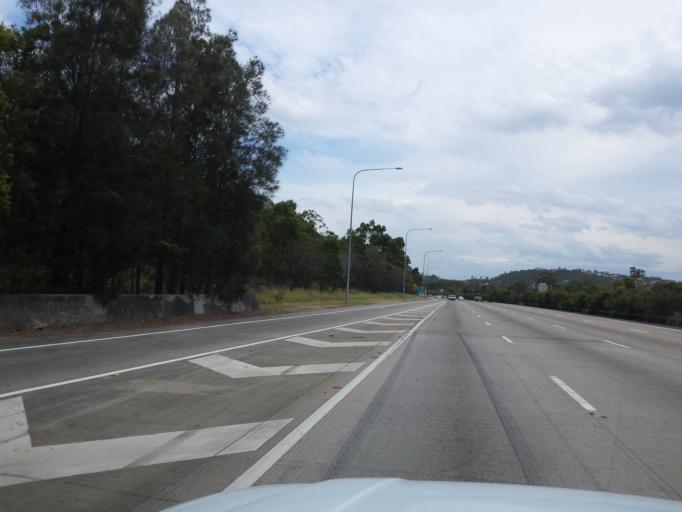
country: AU
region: Queensland
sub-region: Gold Coast
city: Oxenford
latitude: -27.9100
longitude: 153.3184
